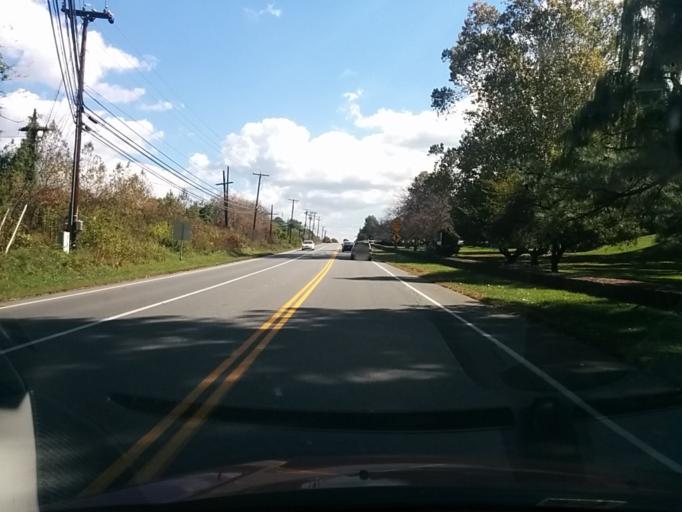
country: US
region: Virginia
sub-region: City of Charlottesville
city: Charlottesville
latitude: 38.0464
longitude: -78.5214
